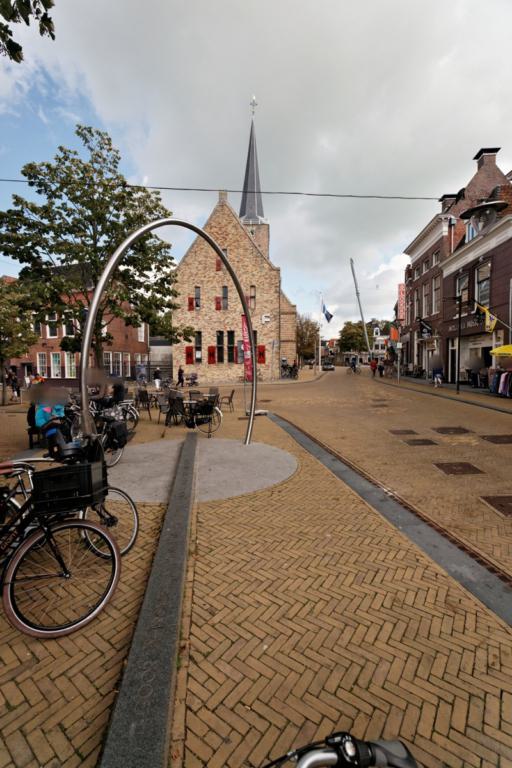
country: NL
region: Friesland
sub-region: Gemeente Franekeradeel
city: Franeker
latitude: 53.1866
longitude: 5.5431
